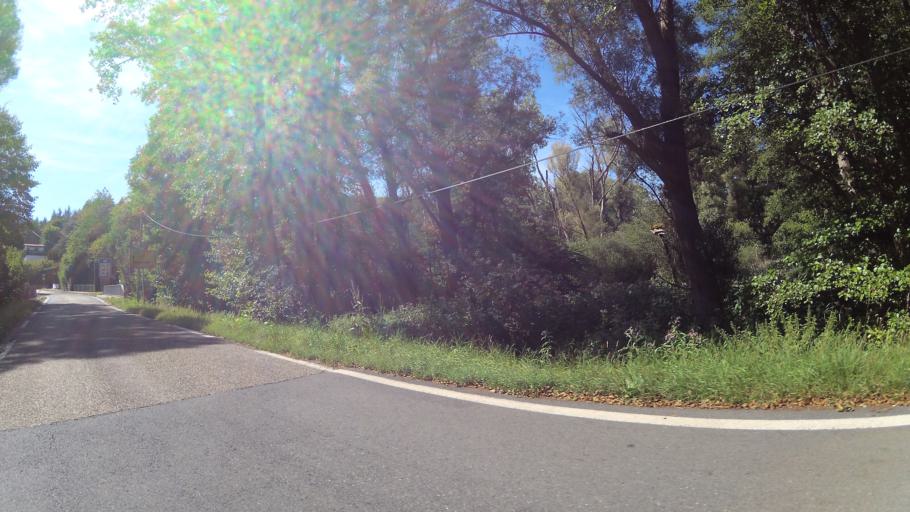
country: DE
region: Rheinland-Pfalz
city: Hornbach
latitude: 49.1521
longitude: 7.3622
